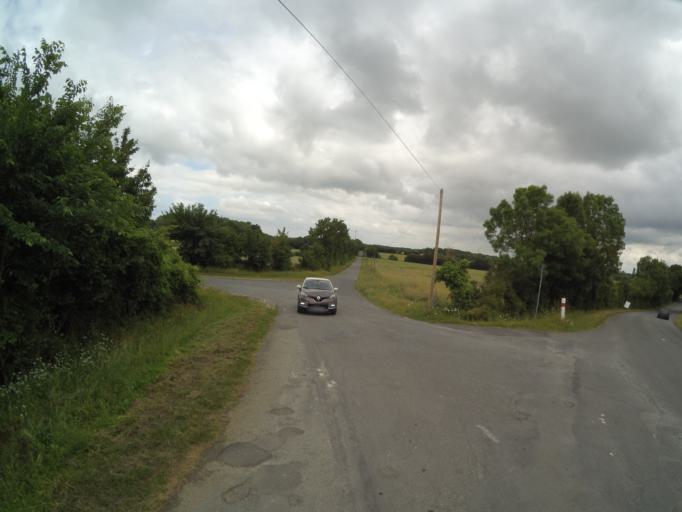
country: FR
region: Poitou-Charentes
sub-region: Departement de la Charente-Maritime
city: Breuil-Magne
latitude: 45.9658
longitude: -0.9701
